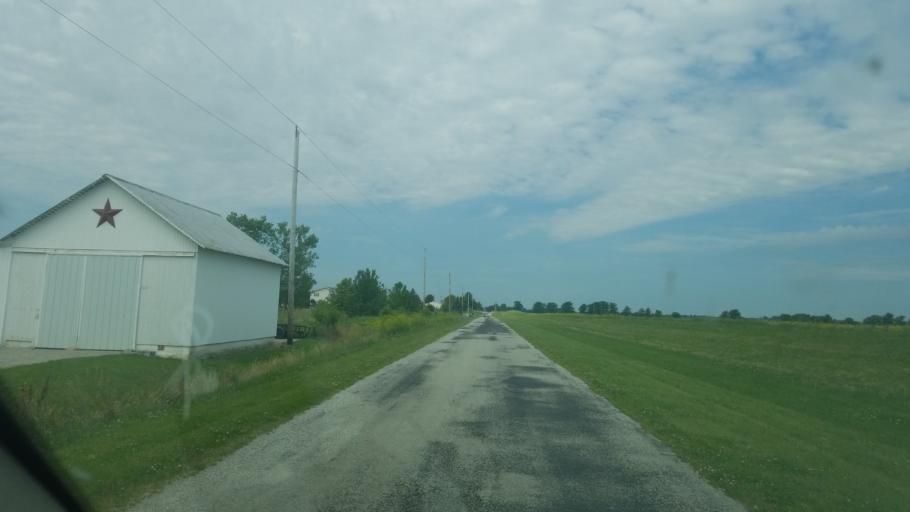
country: US
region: Ohio
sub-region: Wood County
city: North Baltimore
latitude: 41.2322
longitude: -83.5757
